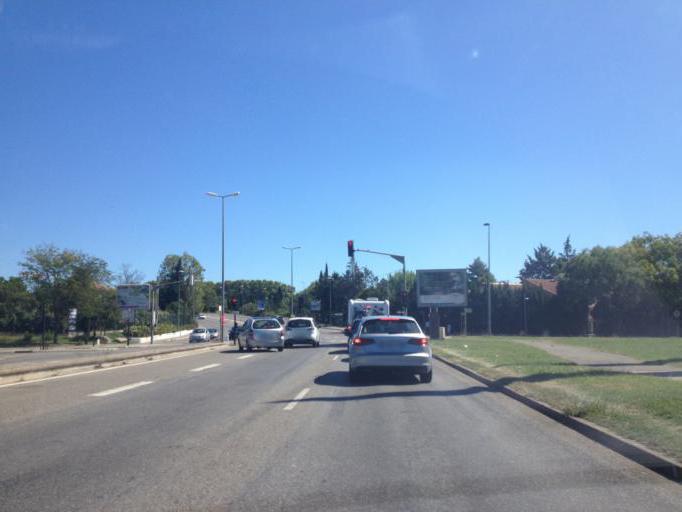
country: FR
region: Provence-Alpes-Cote d'Azur
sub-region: Departement des Bouches-du-Rhone
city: Aix-en-Provence
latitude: 43.5289
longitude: 5.4232
